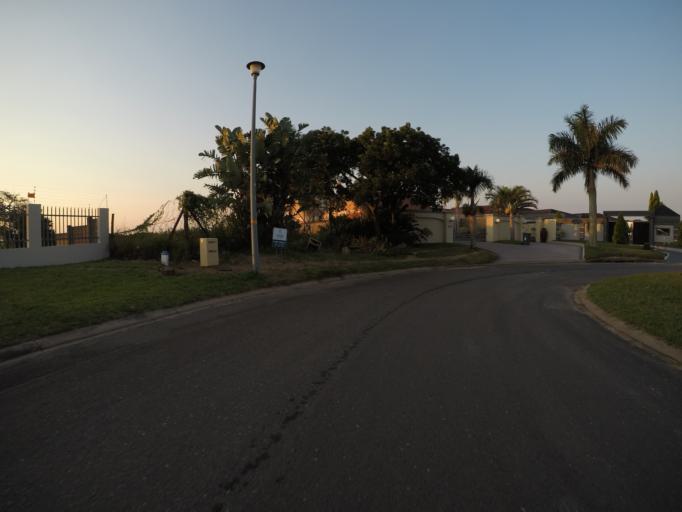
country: ZA
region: KwaZulu-Natal
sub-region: uThungulu District Municipality
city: Richards Bay
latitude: -28.7637
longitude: 32.1161
